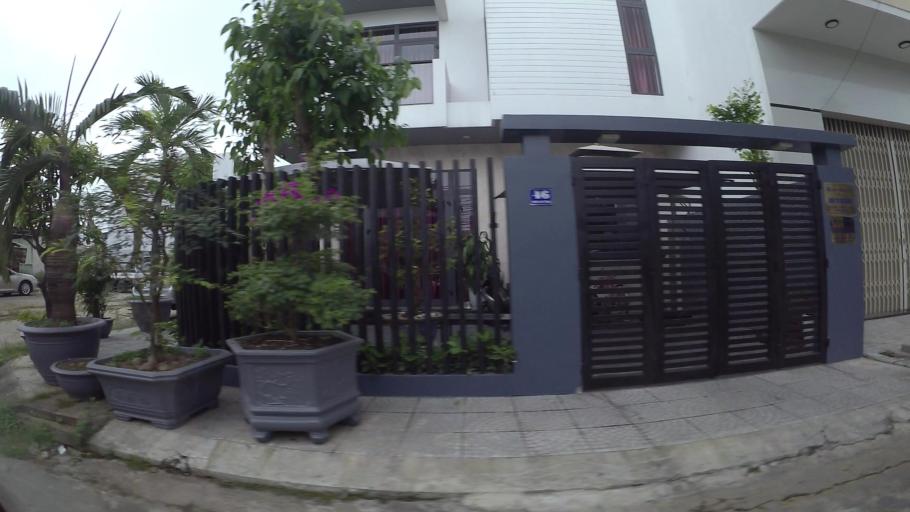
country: VN
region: Da Nang
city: Lien Chieu
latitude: 16.0550
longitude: 108.1666
